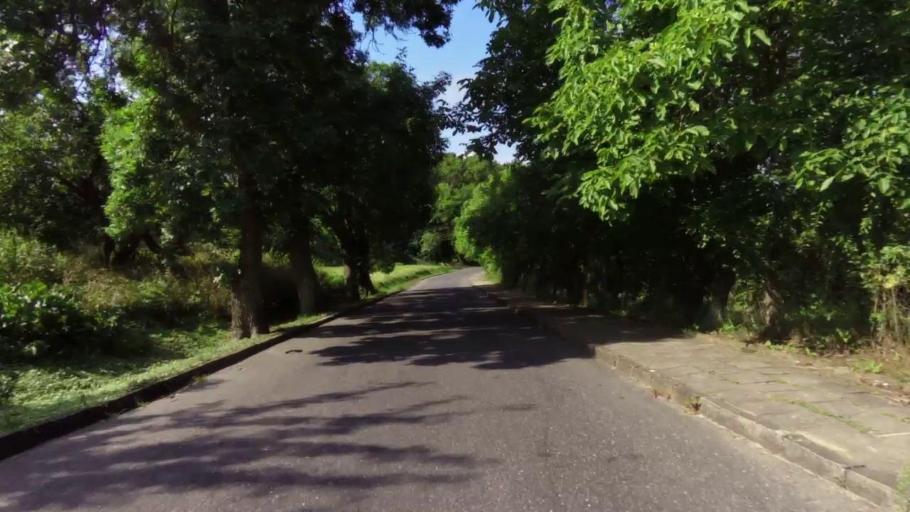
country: PL
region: West Pomeranian Voivodeship
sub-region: Powiat gryfinski
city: Cedynia
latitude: 52.8733
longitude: 14.2003
